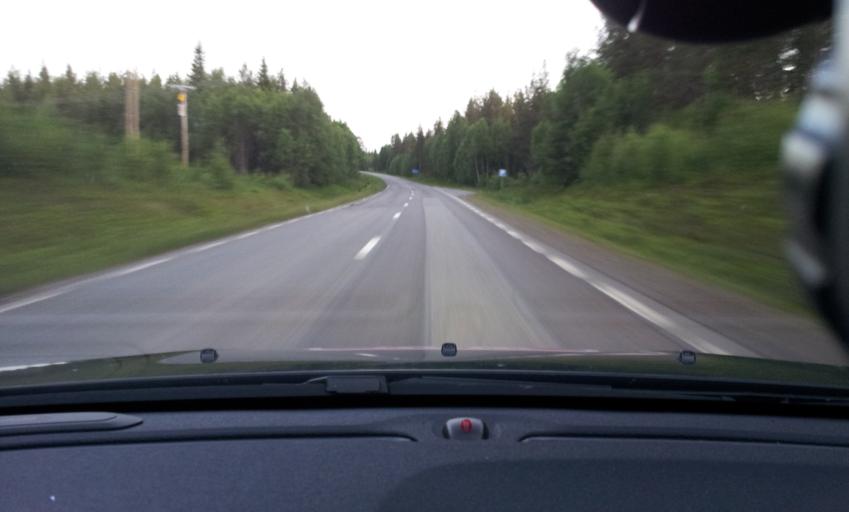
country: SE
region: Jaemtland
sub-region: Ragunda Kommun
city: Hammarstrand
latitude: 62.9947
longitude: 16.1015
